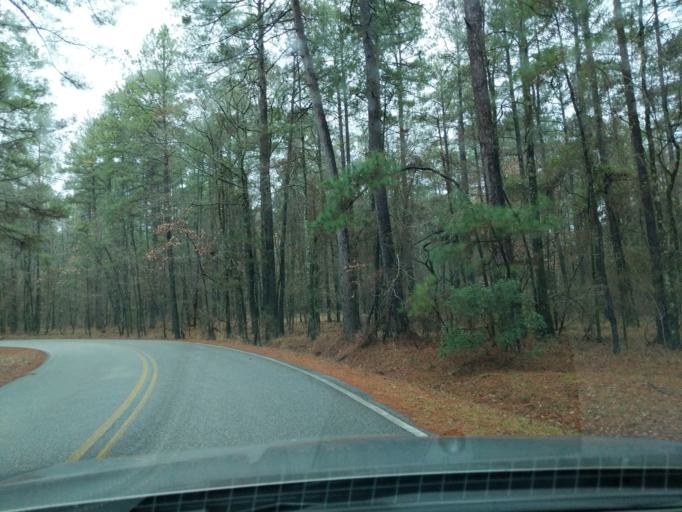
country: US
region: Georgia
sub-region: Columbia County
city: Appling
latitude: 33.6449
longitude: -82.3876
